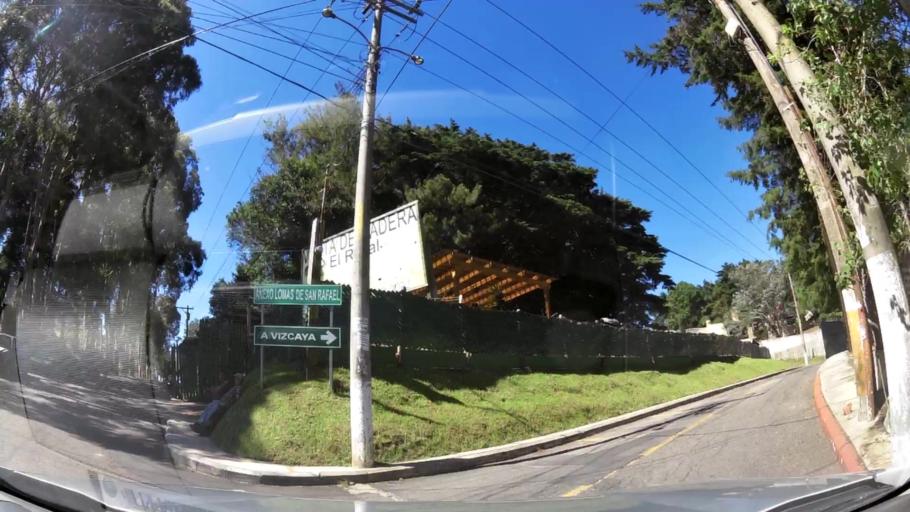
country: GT
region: Guatemala
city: San Jose Pinula
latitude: 14.5394
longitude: -90.4555
